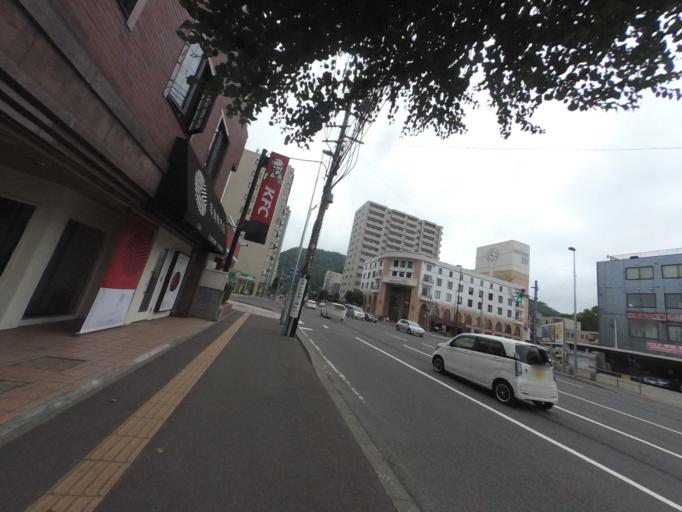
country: JP
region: Hokkaido
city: Sapporo
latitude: 43.0557
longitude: 141.3160
